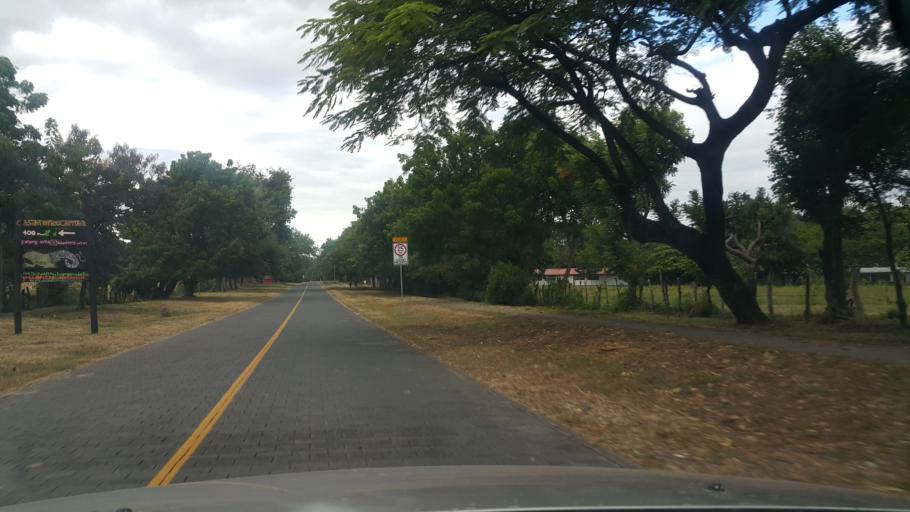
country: NI
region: Rivas
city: Moyogalpa
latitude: 11.4989
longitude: -85.6979
